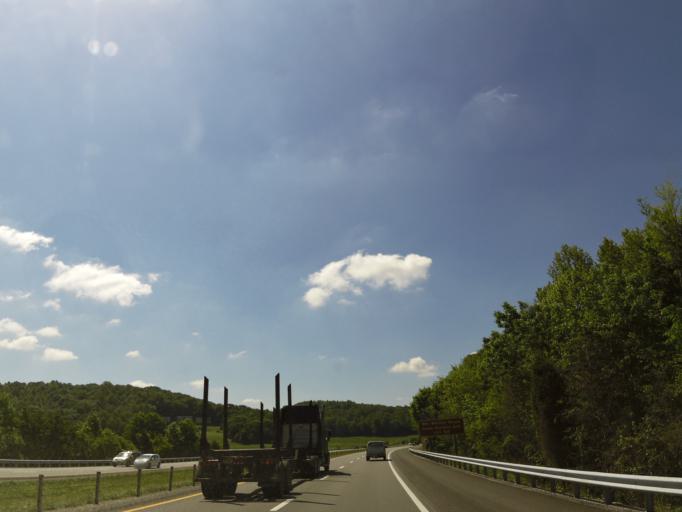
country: US
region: Kentucky
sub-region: Rockcastle County
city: Mount Vernon
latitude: 37.3632
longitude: -84.3096
